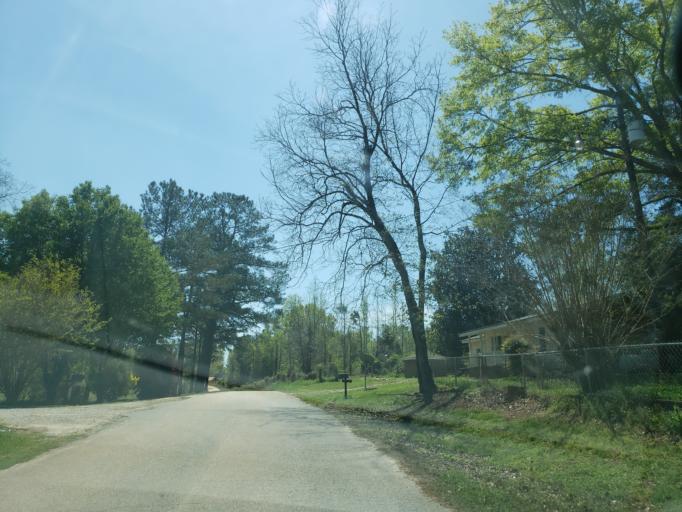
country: US
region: Alabama
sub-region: Tallapoosa County
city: Camp Hill
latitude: 32.6841
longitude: -85.6694
